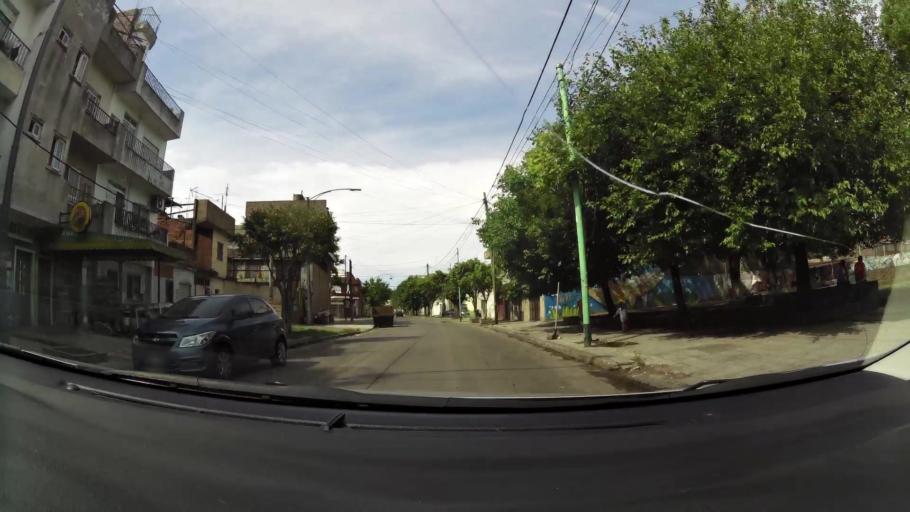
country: AR
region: Buenos Aires F.D.
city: Villa Lugano
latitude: -34.6533
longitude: -58.4319
